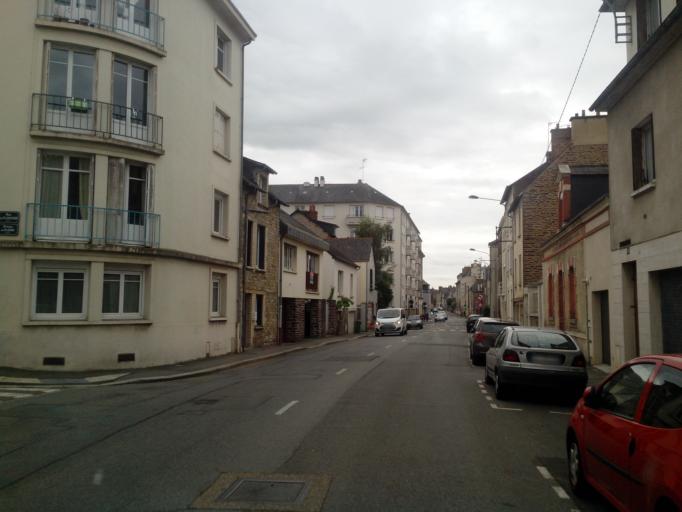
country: FR
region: Brittany
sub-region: Departement d'Ille-et-Vilaine
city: Rennes
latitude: 48.0996
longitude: -1.6720
